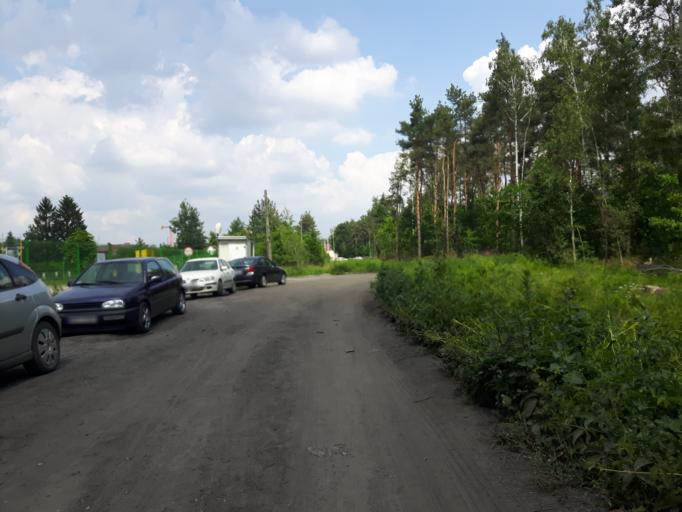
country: PL
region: Masovian Voivodeship
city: Zielonka
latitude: 52.2836
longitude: 21.1395
